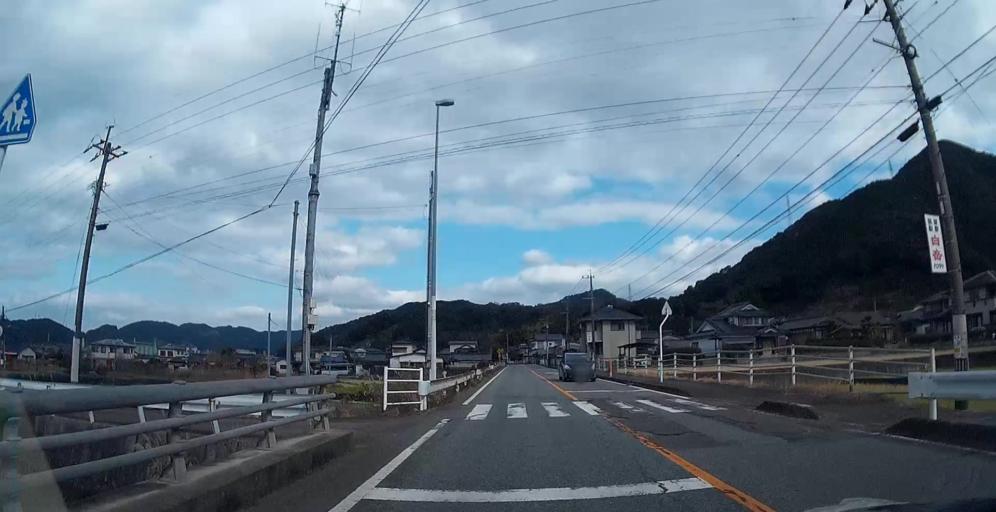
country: JP
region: Kumamoto
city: Minamata
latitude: 32.3438
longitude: 130.5010
